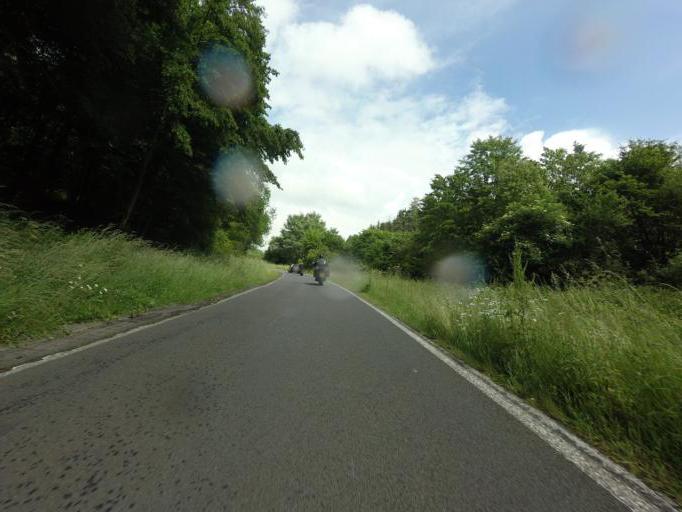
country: DE
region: Rheinland-Pfalz
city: Kottenborn
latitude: 50.3605
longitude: 6.8959
